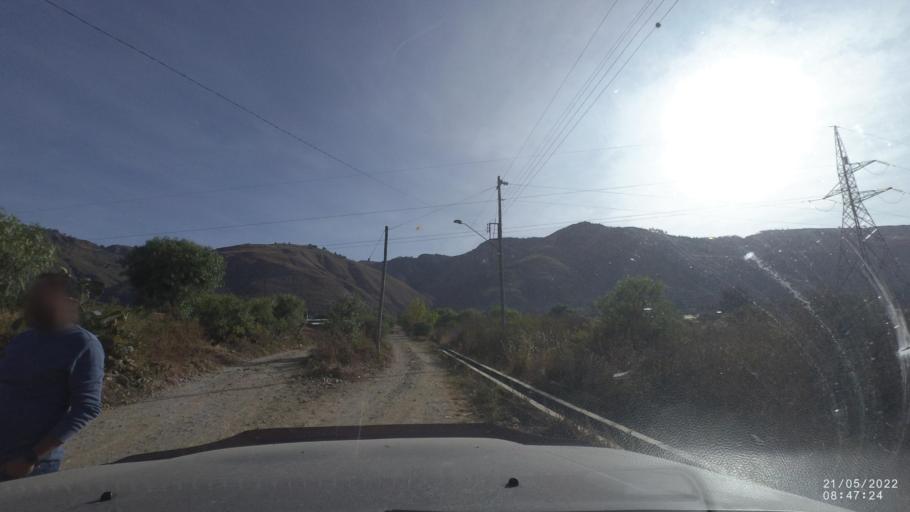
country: BO
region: Cochabamba
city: Cochabamba
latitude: -17.3816
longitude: -66.0413
